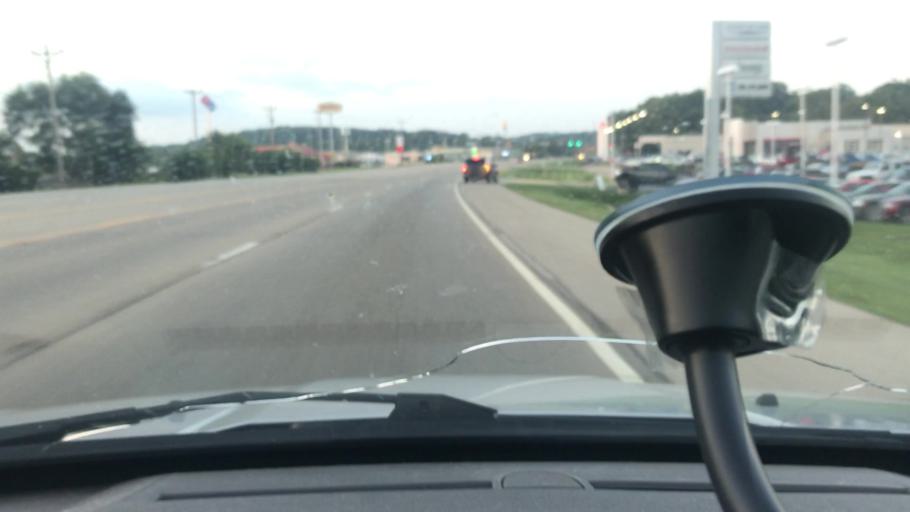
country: US
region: Illinois
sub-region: Tazewell County
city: North Pekin
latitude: 40.6230
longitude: -89.6225
